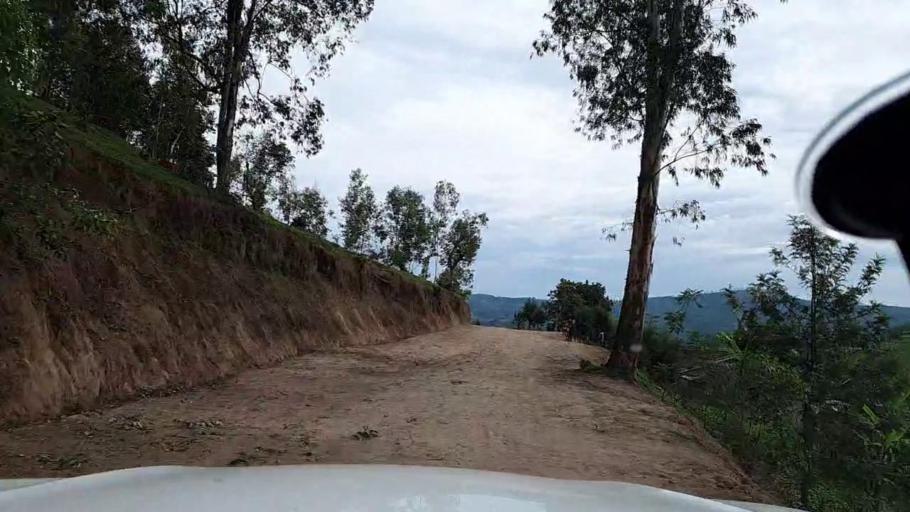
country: RW
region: Southern Province
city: Gitarama
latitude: -2.1284
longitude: 29.6606
